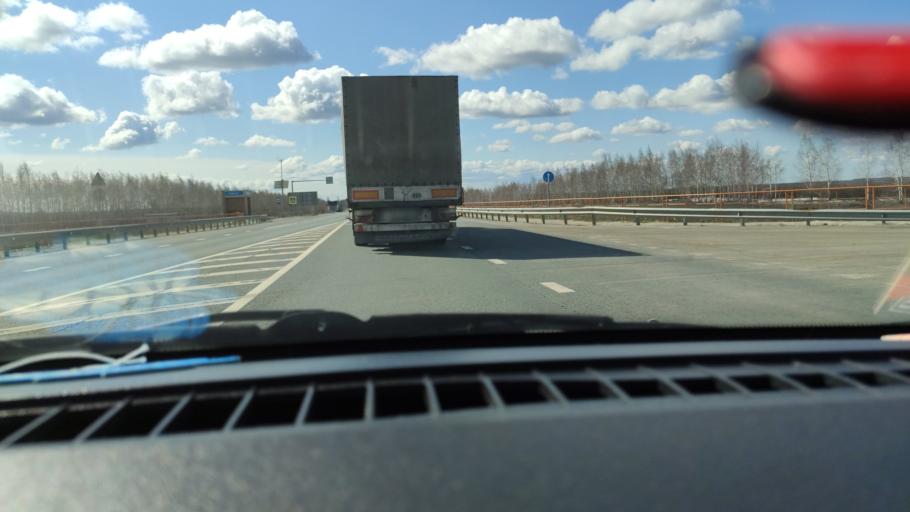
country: RU
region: Samara
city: Syzran'
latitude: 52.9193
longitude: 48.3022
